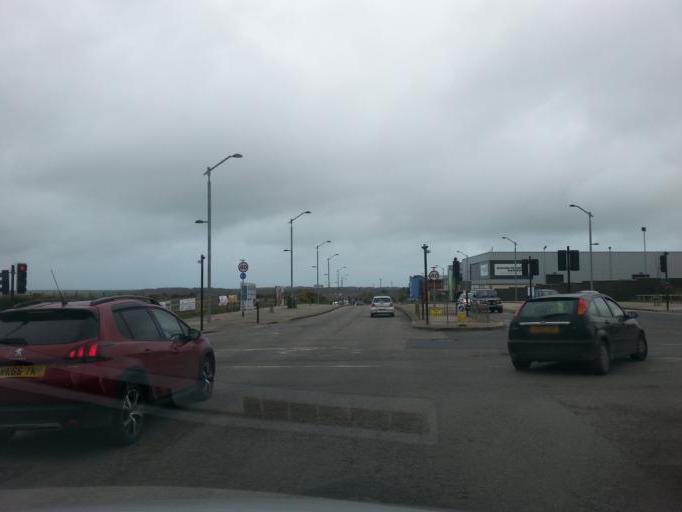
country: GB
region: England
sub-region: Cornwall
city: Camborne
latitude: 50.2250
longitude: -5.2774
